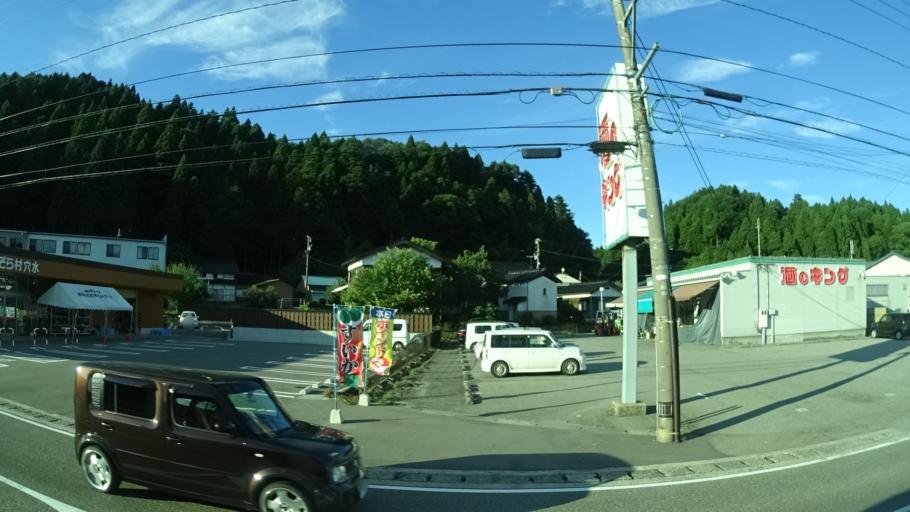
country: JP
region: Ishikawa
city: Nanao
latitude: 37.2447
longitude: 136.8978
